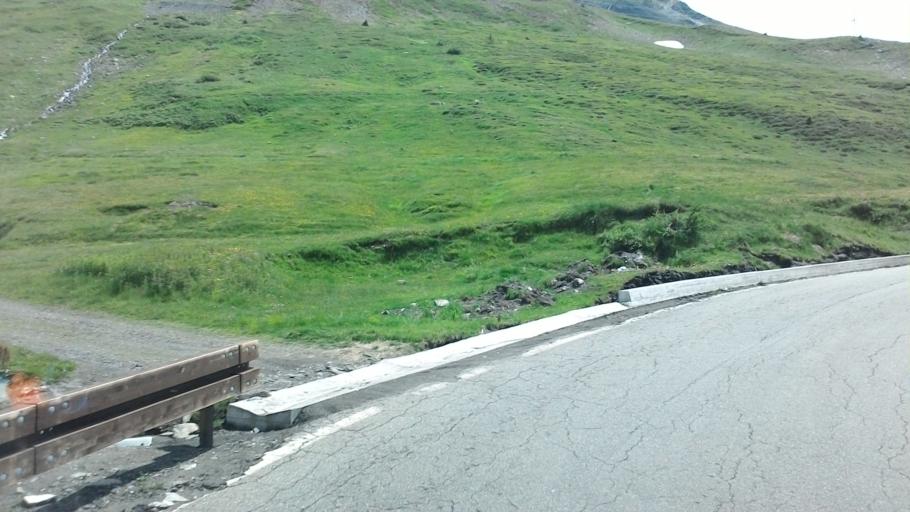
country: IT
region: Aosta Valley
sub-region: Valle d'Aosta
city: La Thuile
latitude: 45.6910
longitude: 6.8916
